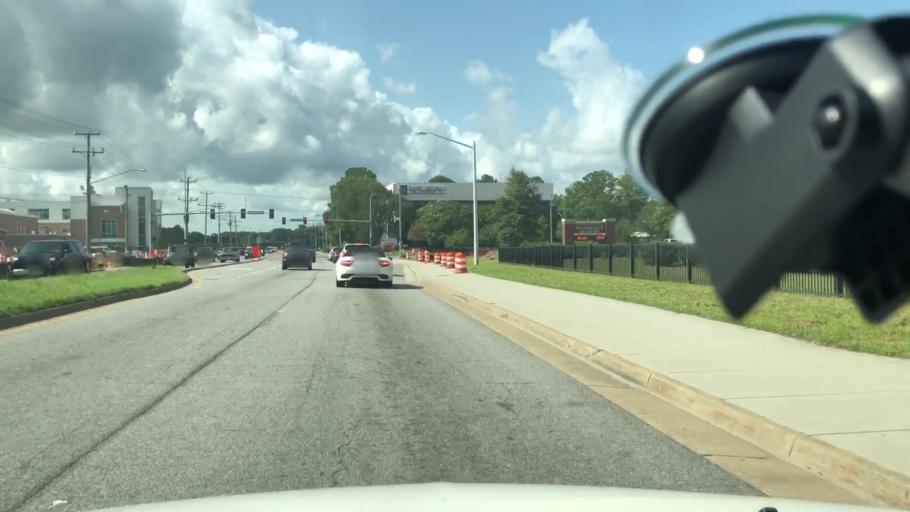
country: US
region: Virginia
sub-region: City of Chesapeake
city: Chesapeake
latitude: 36.8433
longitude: -76.1579
